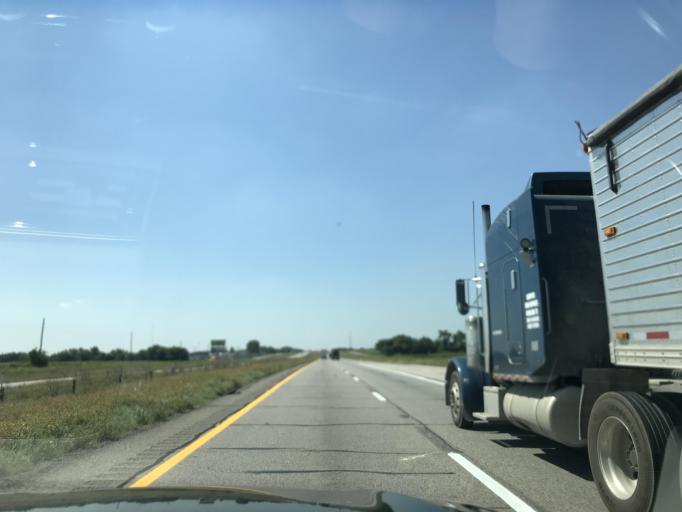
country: US
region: Texas
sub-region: Johnson County
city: Alvarado
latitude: 32.3489
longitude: -97.1951
